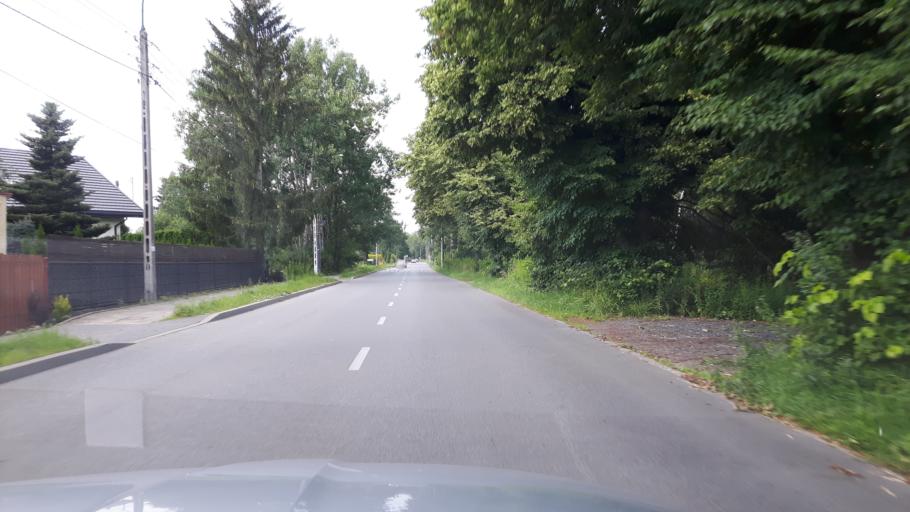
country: PL
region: Masovian Voivodeship
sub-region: Warszawa
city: Rembertow
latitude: 52.2825
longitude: 21.1719
